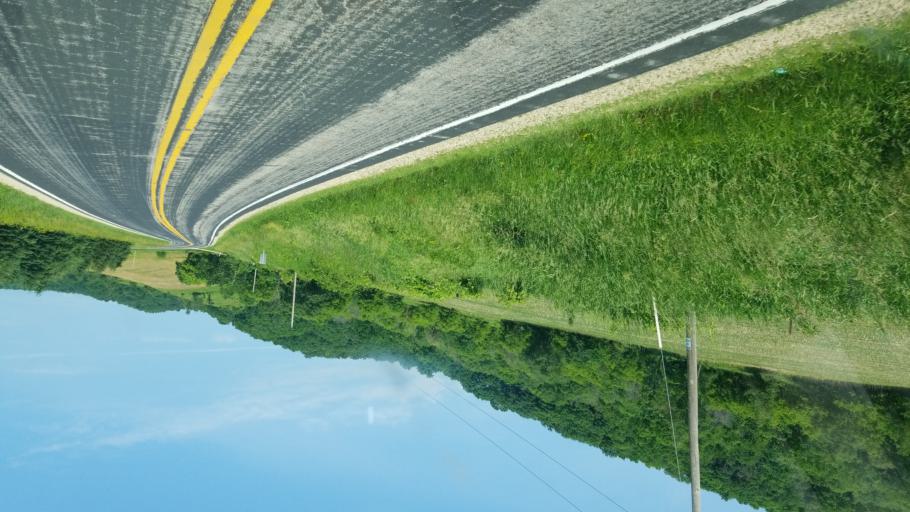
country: US
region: Wisconsin
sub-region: Monroe County
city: Cashton
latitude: 43.5747
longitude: -90.6041
